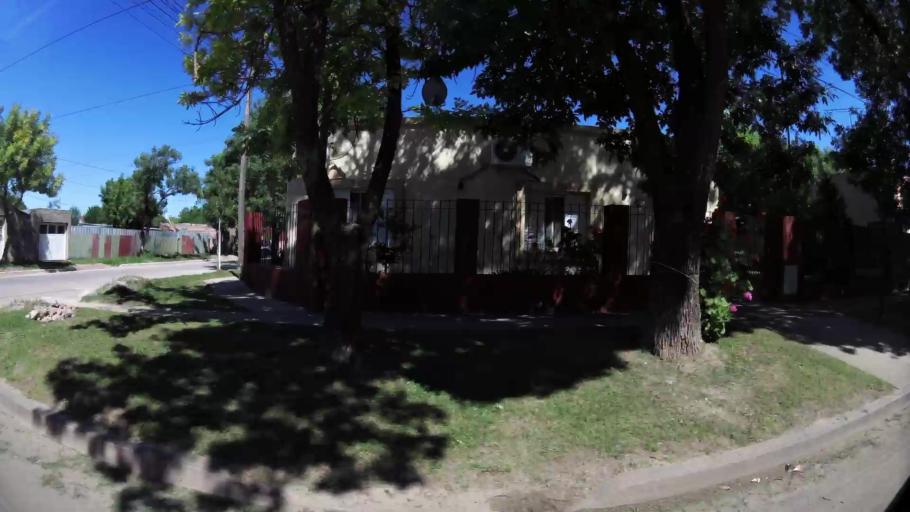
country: AR
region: Santa Fe
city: Esperanza
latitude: -31.4338
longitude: -60.9247
